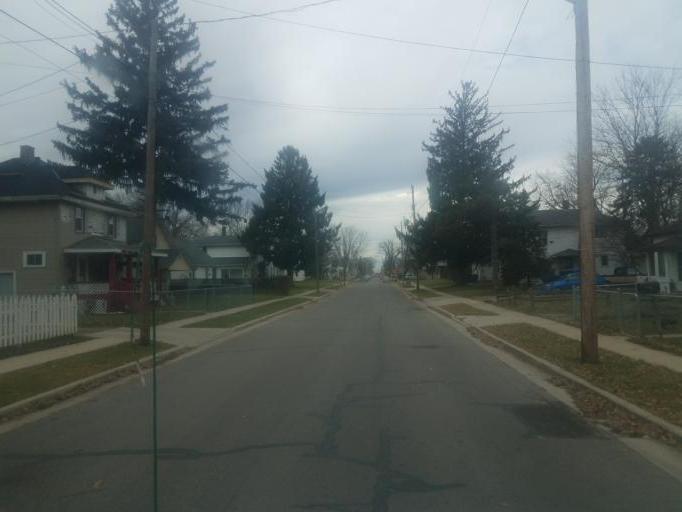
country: US
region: Ohio
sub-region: Marion County
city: Marion
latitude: 40.5904
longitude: -83.0994
